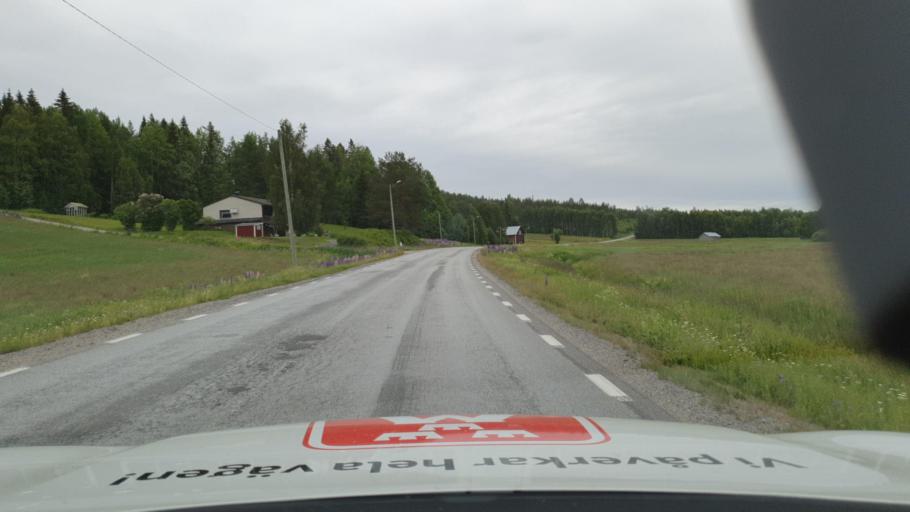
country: SE
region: Vaesterbotten
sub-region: Nordmalings Kommun
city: Nordmaling
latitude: 63.6267
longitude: 19.4243
